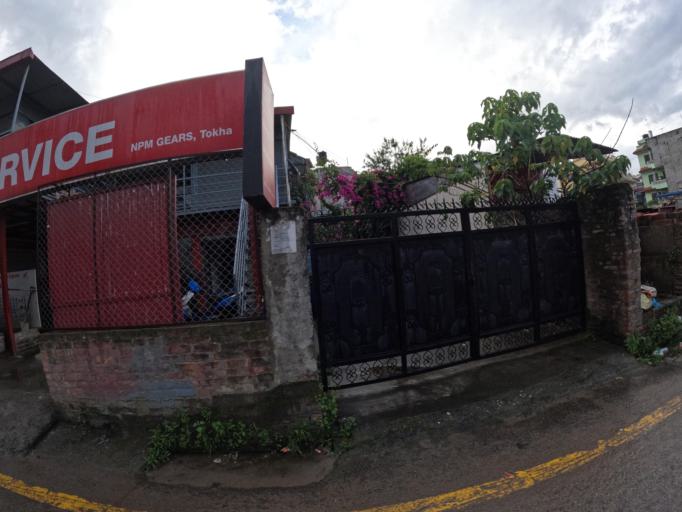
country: NP
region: Central Region
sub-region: Bagmati Zone
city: Kathmandu
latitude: 27.7459
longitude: 85.3238
